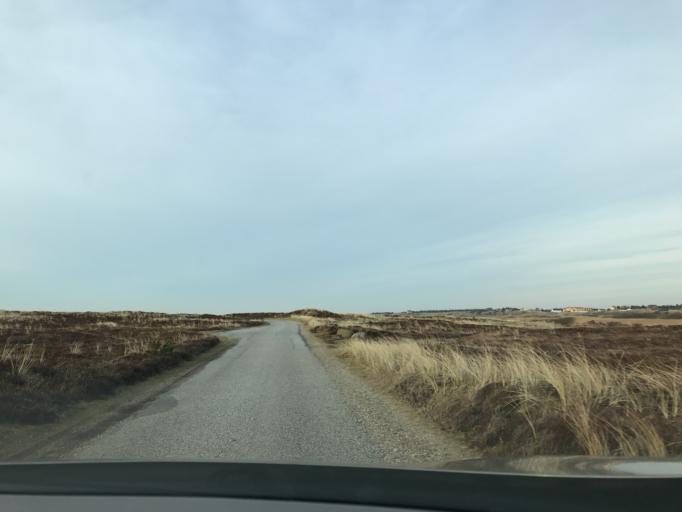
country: DK
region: Central Jutland
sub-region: Ringkobing-Skjern Kommune
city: Hvide Sande
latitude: 55.8071
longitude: 8.1810
